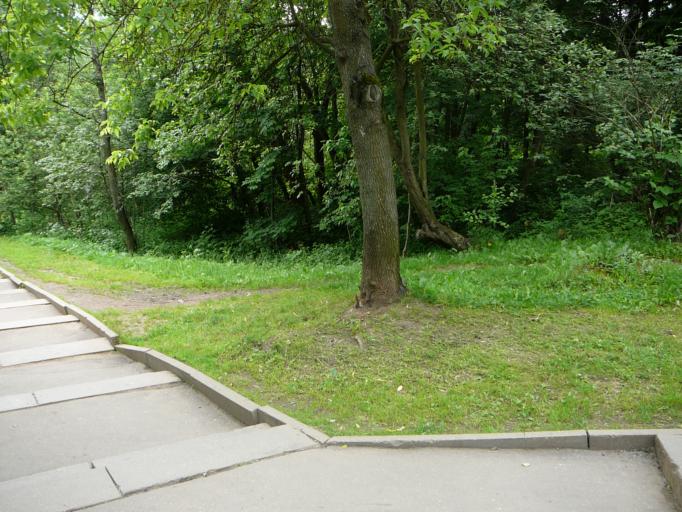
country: RU
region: Moskovskaya
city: Arkhangel'skoye
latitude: 55.8135
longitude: 37.3046
